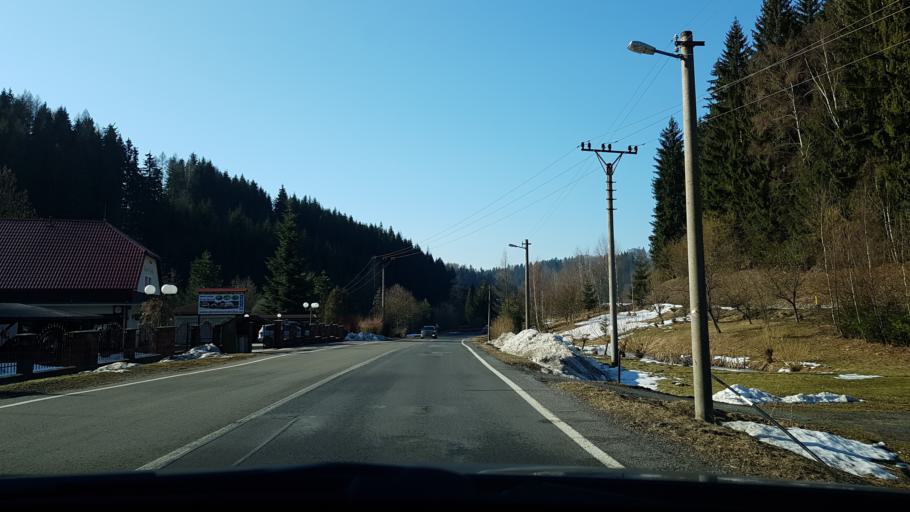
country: CZ
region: Olomoucky
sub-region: Okres Sumperk
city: Hanusovice
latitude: 50.1126
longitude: 17.0049
